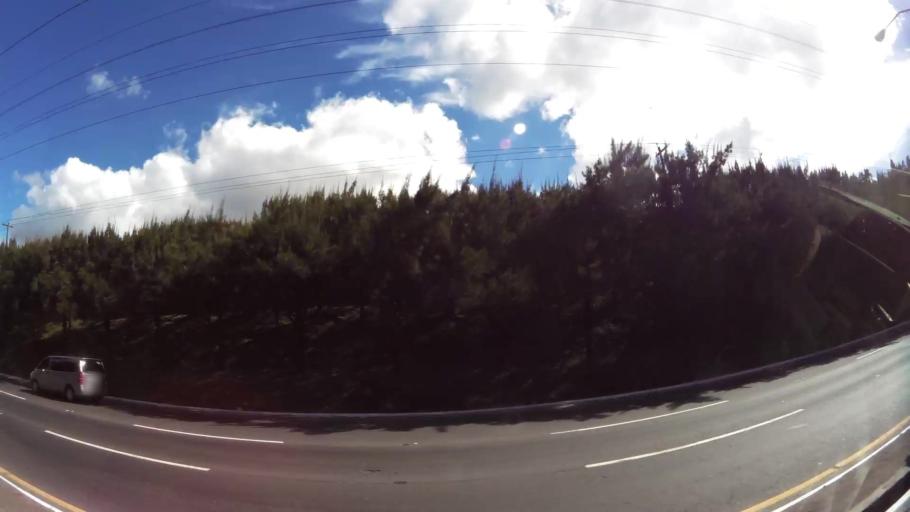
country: GT
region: Guatemala
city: Guatemala City
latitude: 14.6410
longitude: -90.5472
